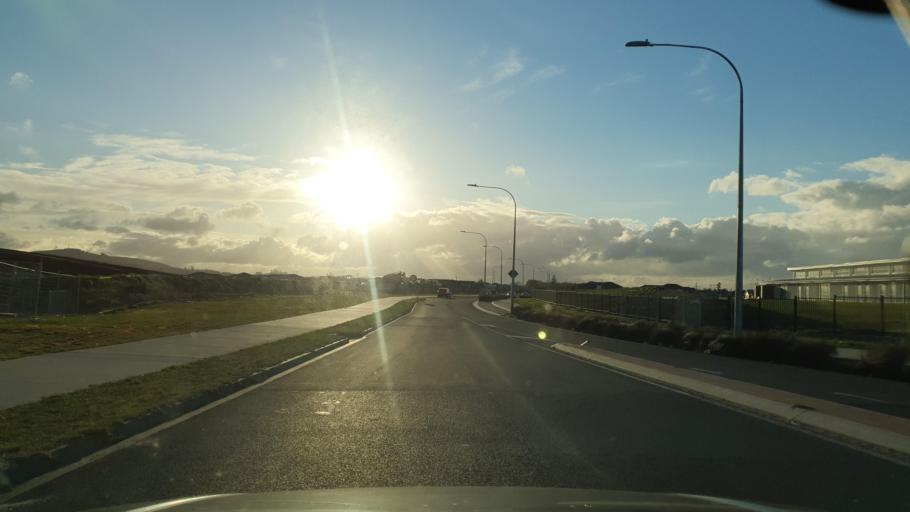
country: NZ
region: Bay of Plenty
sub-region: Western Bay of Plenty District
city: Maketu
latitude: -37.7223
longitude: 176.3199
